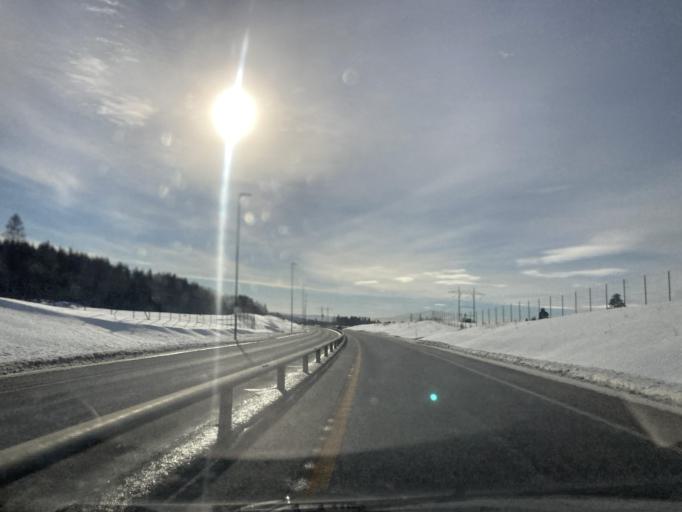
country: NO
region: Hedmark
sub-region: Loten
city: Loten
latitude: 60.8162
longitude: 11.2853
